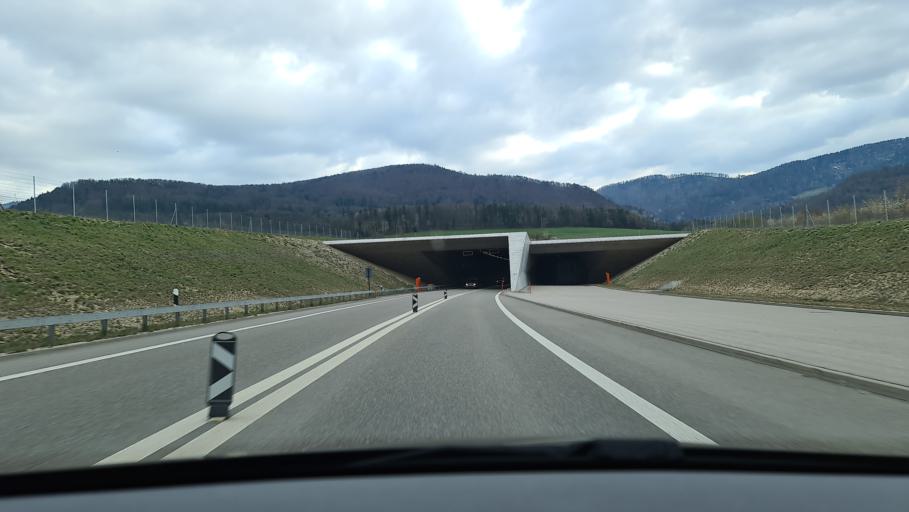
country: CH
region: Jura
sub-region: Delemont District
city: Courrendlin
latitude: 47.3451
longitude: 7.3817
